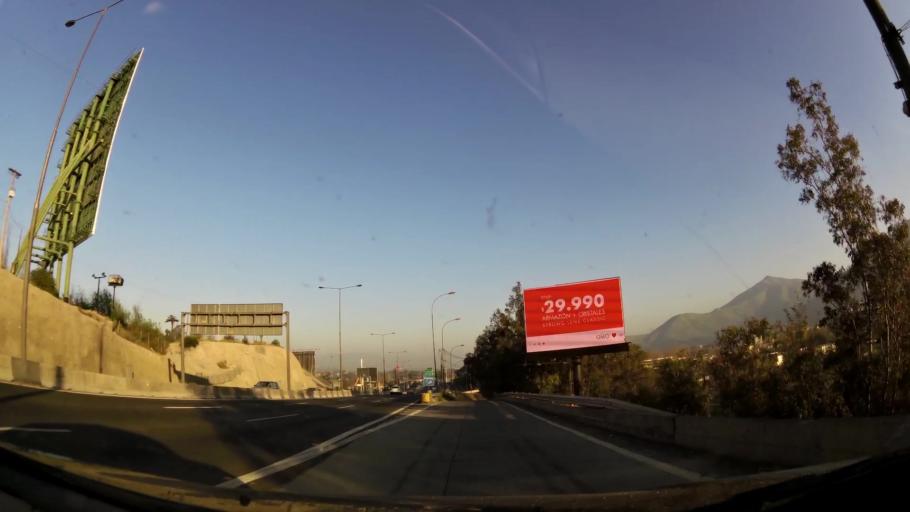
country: CL
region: Santiago Metropolitan
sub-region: Provincia de Santiago
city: Santiago
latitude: -33.3962
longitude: -70.6203
